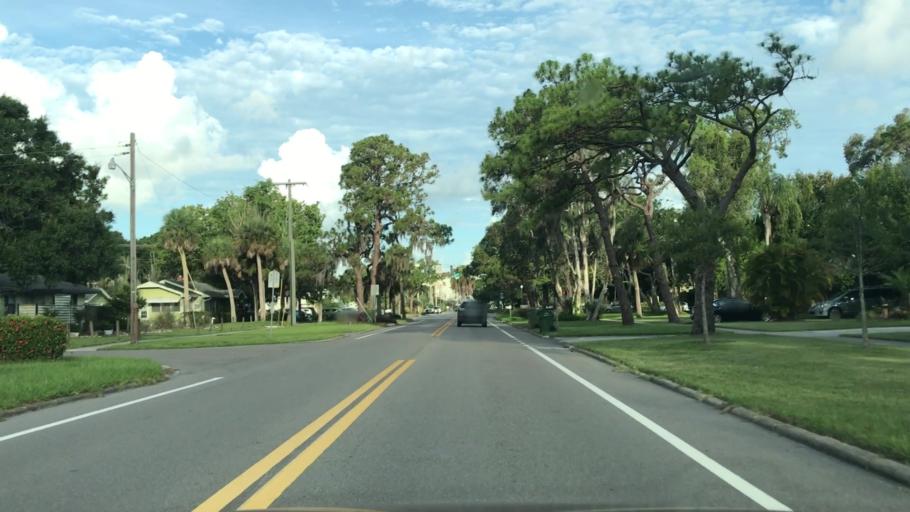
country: US
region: Florida
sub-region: Sarasota County
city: Sarasota
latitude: 27.3356
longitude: -82.5210
